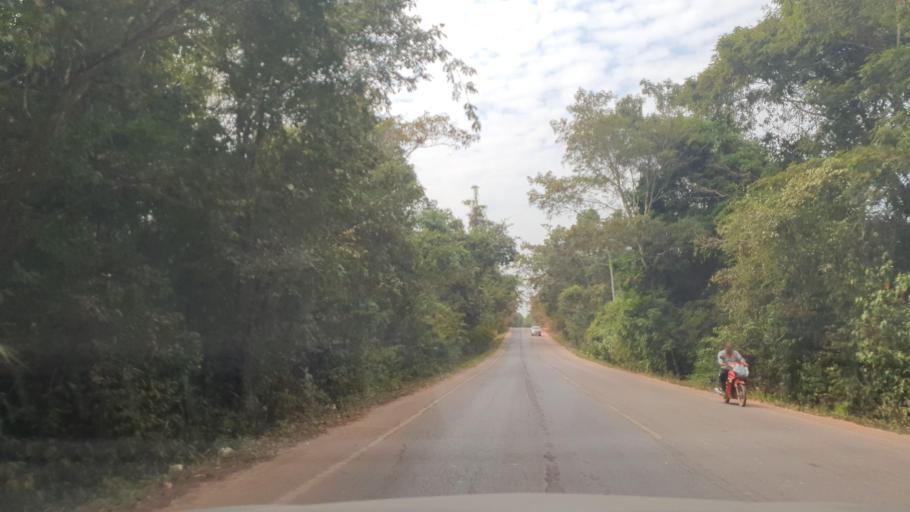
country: TH
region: Changwat Bueng Kan
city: Bung Khla
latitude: 18.3006
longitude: 103.9492
